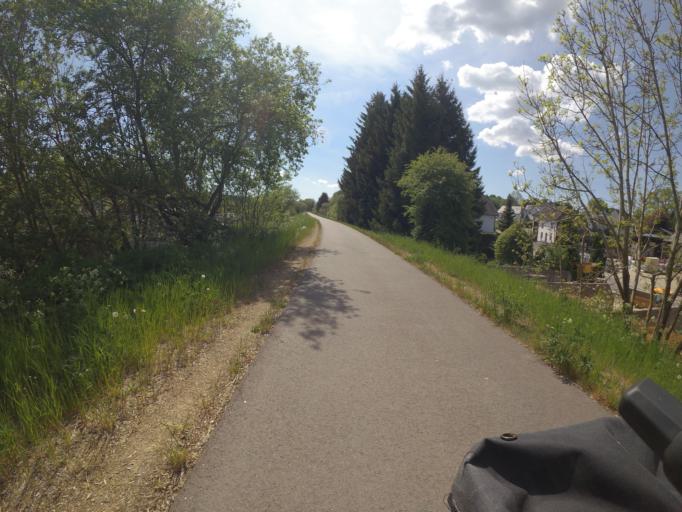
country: BE
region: Wallonia
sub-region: Province de Liege
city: Bullange
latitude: 50.4094
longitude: 6.2628
